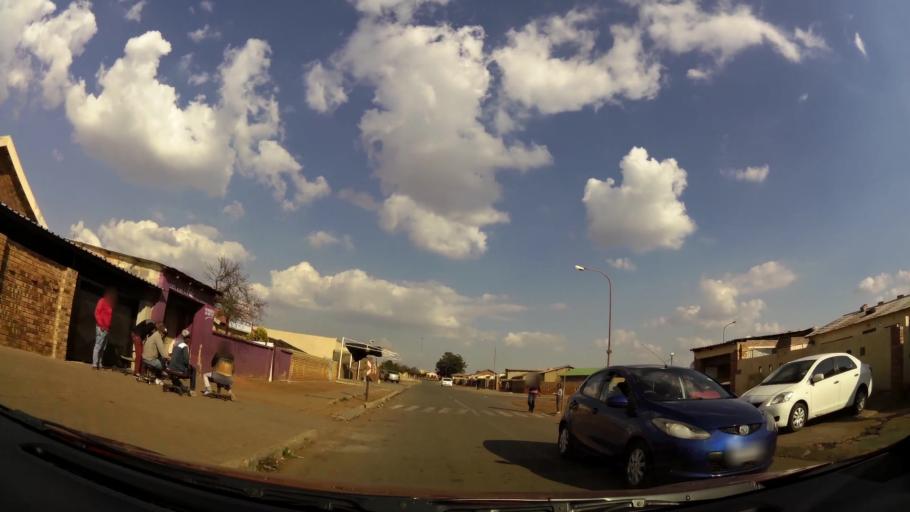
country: ZA
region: Gauteng
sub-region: City of Johannesburg Metropolitan Municipality
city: Soweto
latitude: -26.2264
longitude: 27.8693
